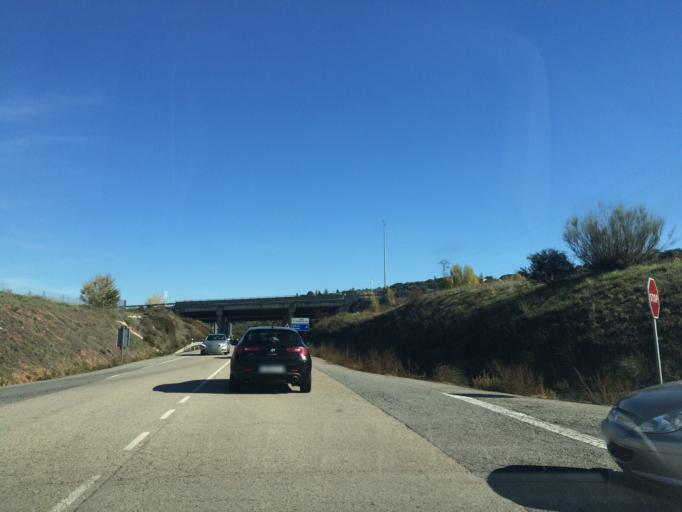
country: ES
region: Madrid
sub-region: Provincia de Madrid
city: Venturada
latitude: 40.7916
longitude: -3.6193
